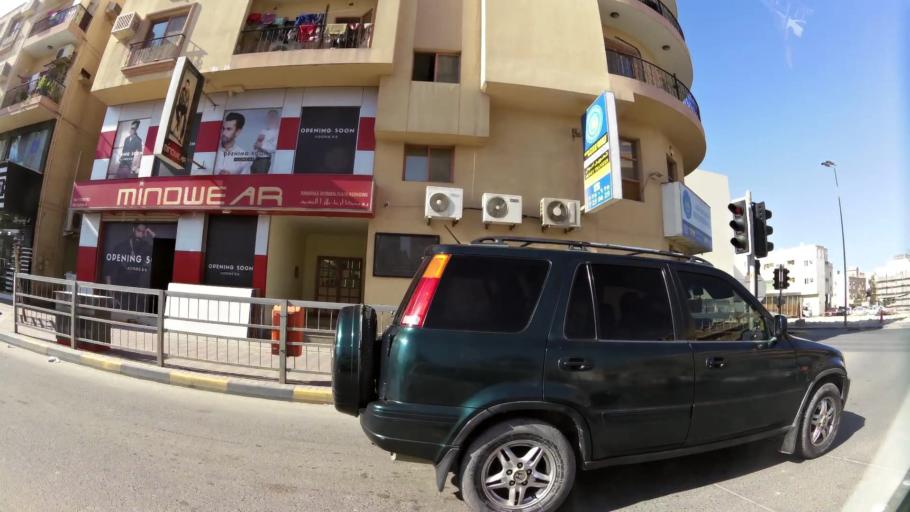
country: BH
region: Manama
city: Manama
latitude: 26.2279
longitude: 50.5820
